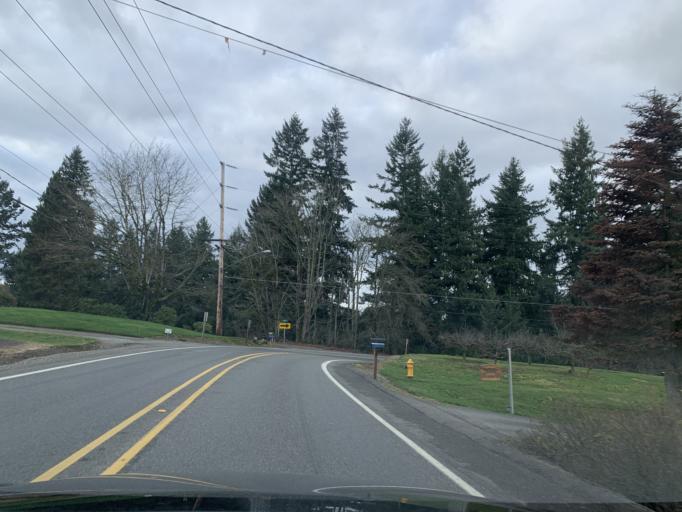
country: US
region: Washington
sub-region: Pierce County
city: Milton
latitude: 47.2356
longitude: -122.3066
